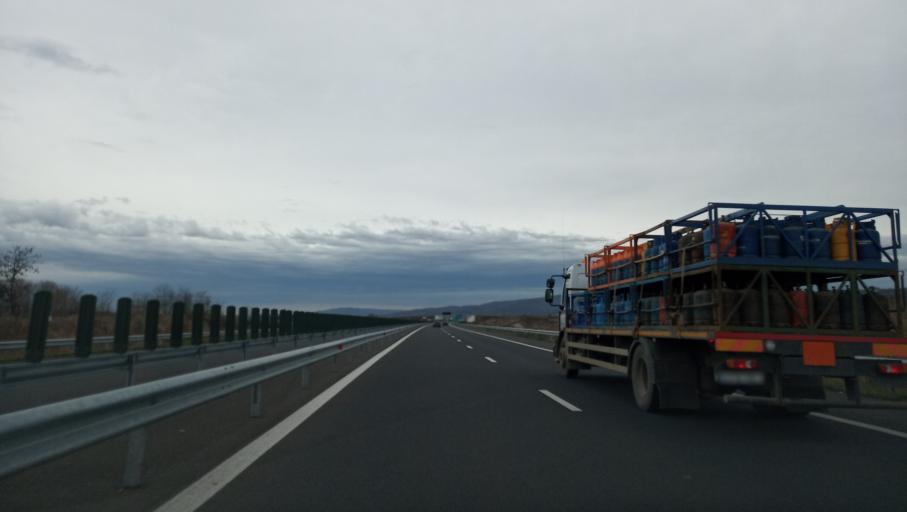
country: RO
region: Hunedoara
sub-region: Comuna Ilia
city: Ilia
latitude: 45.9462
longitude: 22.6804
